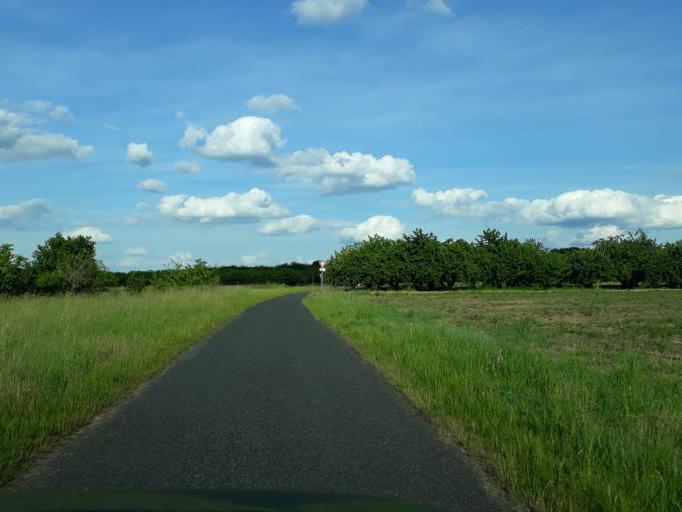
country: FR
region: Centre
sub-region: Departement du Loiret
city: Saint-Hilaire-Saint-Mesmin
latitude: 47.8438
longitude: 1.8207
